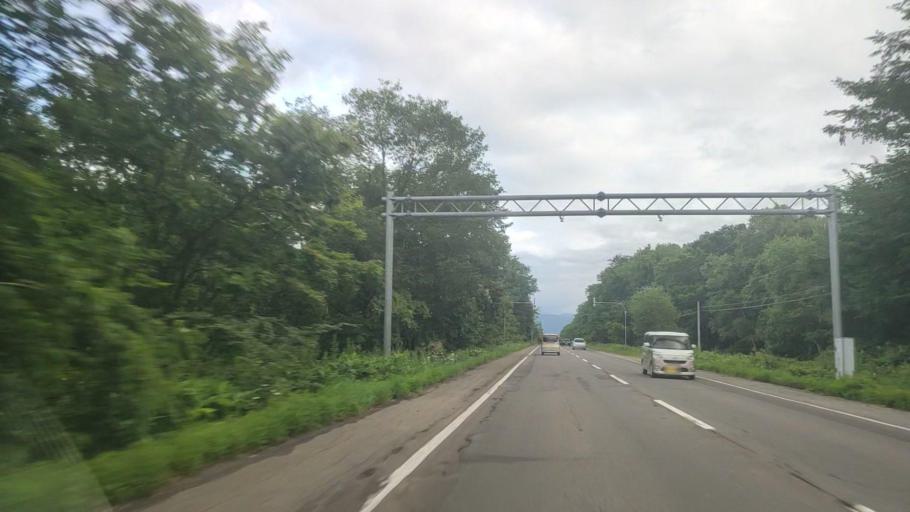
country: JP
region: Hokkaido
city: Nanae
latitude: 42.0164
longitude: 140.6222
